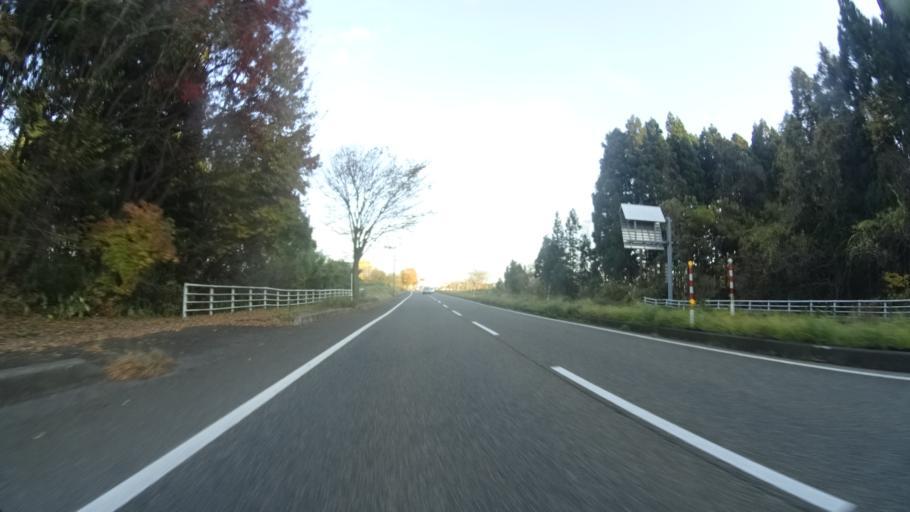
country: JP
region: Niigata
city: Nagaoka
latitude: 37.4503
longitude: 138.7638
